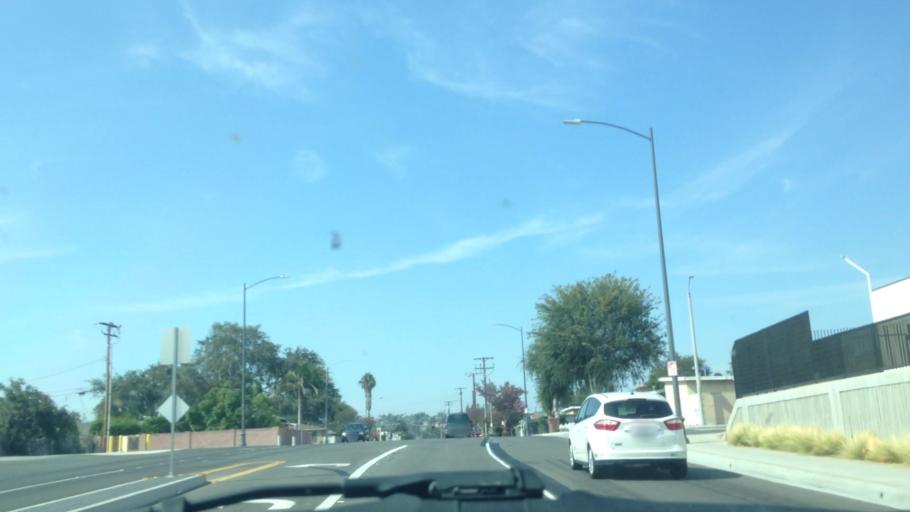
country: US
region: California
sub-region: Orange County
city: Fullerton
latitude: 33.8679
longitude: -117.9069
